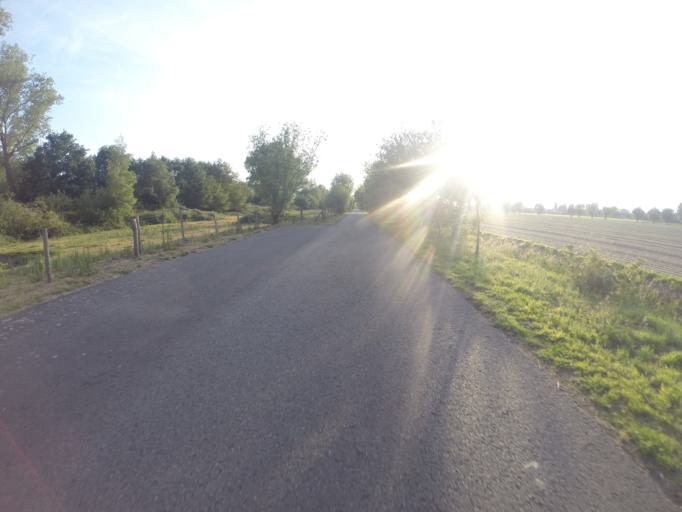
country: BE
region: Flanders
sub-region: Provincie West-Vlaanderen
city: Beernem
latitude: 51.1417
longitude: 3.3189
